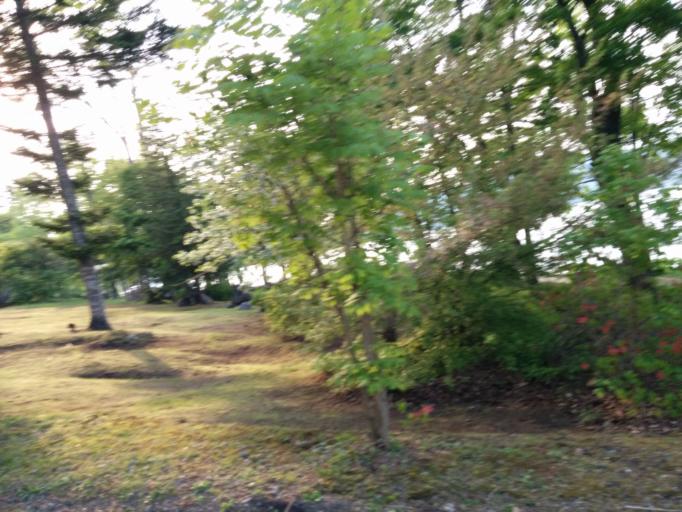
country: JP
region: Hokkaido
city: Bihoro
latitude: 43.4339
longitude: 144.0965
